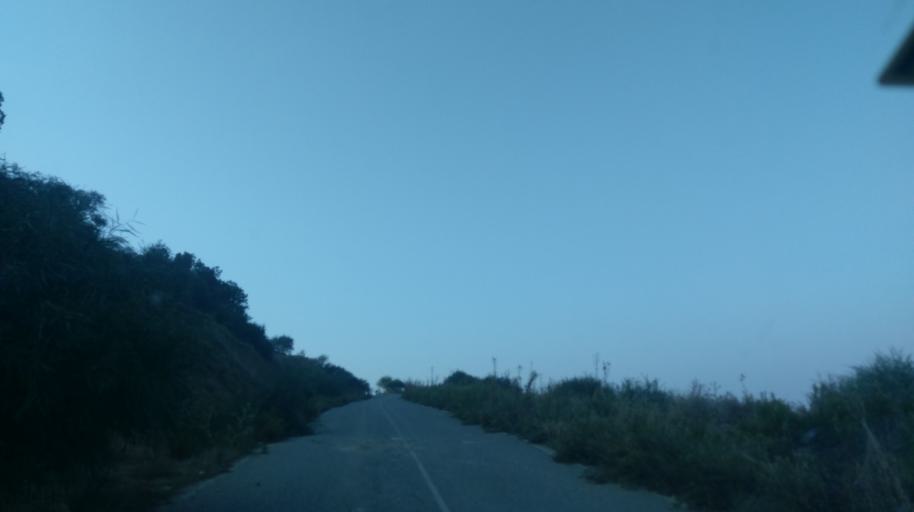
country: CY
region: Ammochostos
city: Trikomo
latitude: 35.4156
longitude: 33.9059
